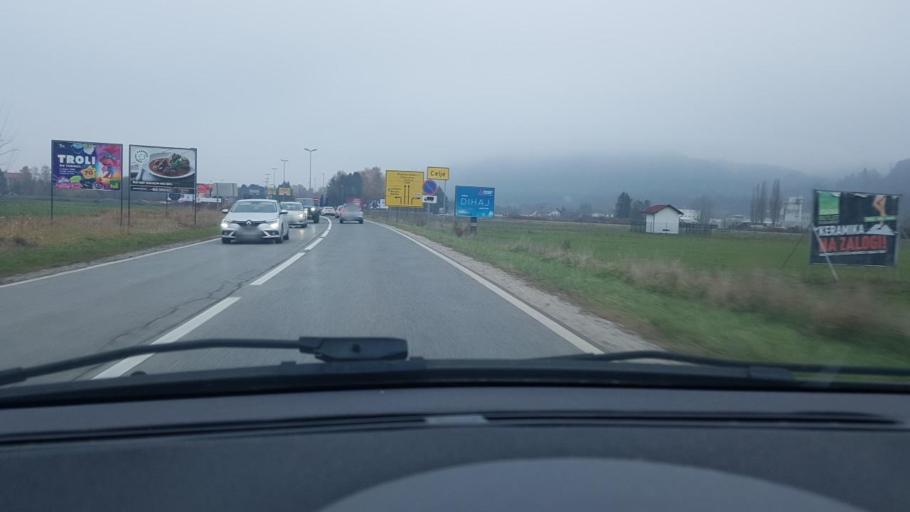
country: SI
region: Celje
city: Celje
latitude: 46.2393
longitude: 15.2256
